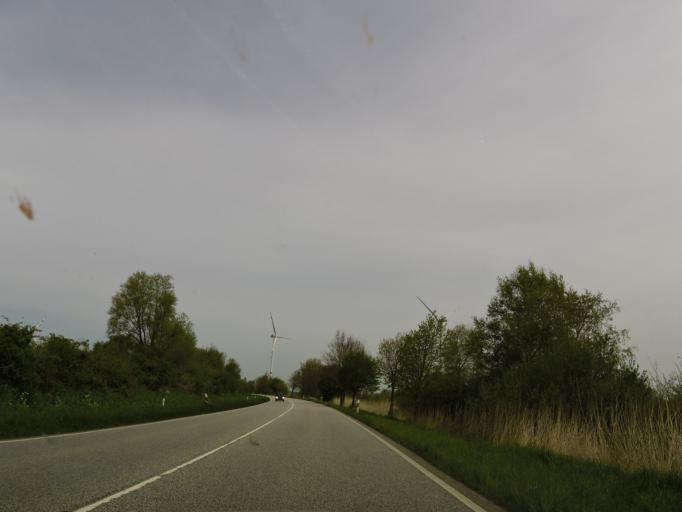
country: DE
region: Schleswig-Holstein
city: Stelle-Wittenwurth
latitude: 54.2438
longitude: 9.0389
